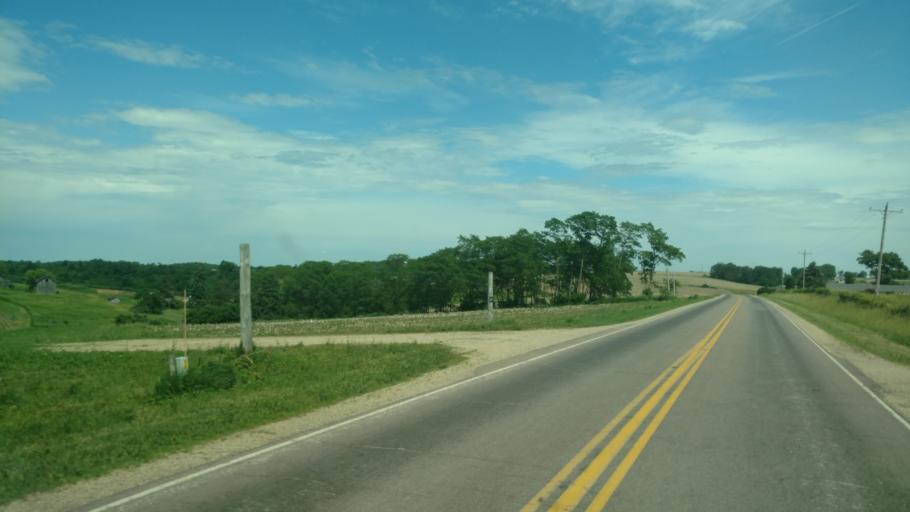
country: US
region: Wisconsin
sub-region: Vernon County
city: Hillsboro
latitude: 43.6511
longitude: -90.4544
